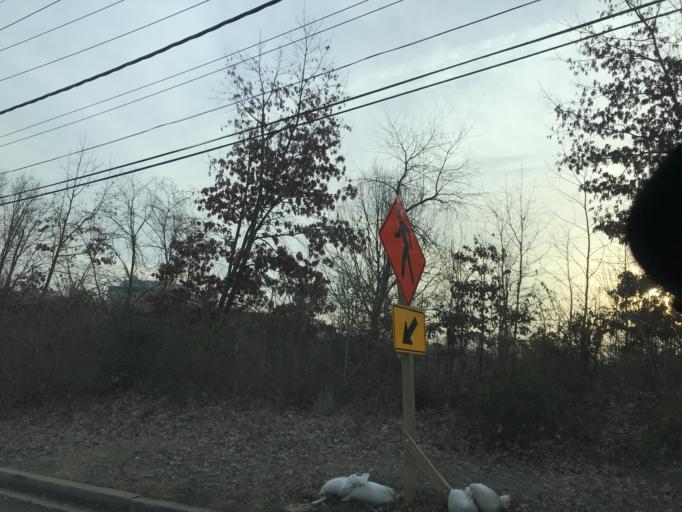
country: US
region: Maryland
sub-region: Prince George's County
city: Woodlawn
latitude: 38.9457
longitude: -76.8784
